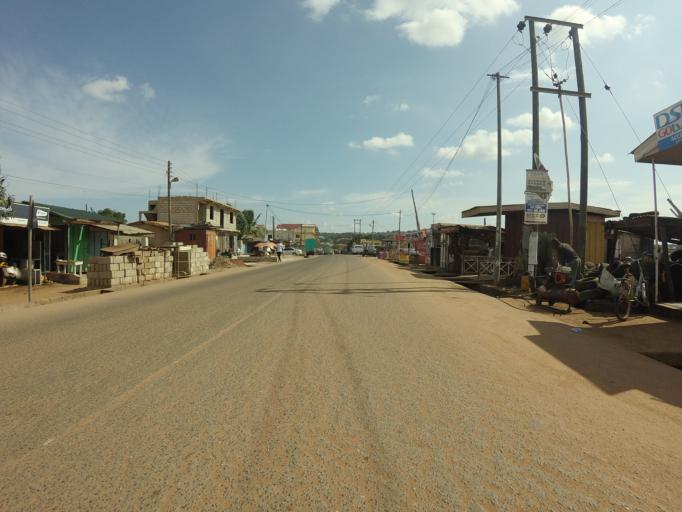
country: GH
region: Greater Accra
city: Medina Estates
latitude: 5.6772
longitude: -0.1814
